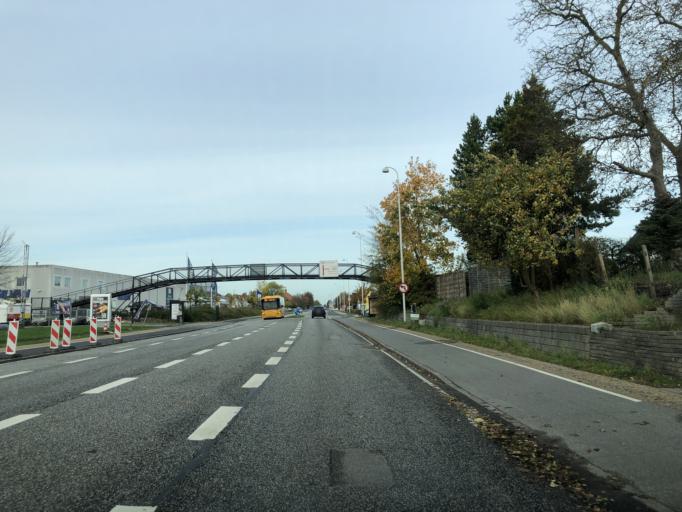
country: DK
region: Capital Region
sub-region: Rudersdal Kommune
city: Birkerod
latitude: 55.8397
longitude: 12.4426
